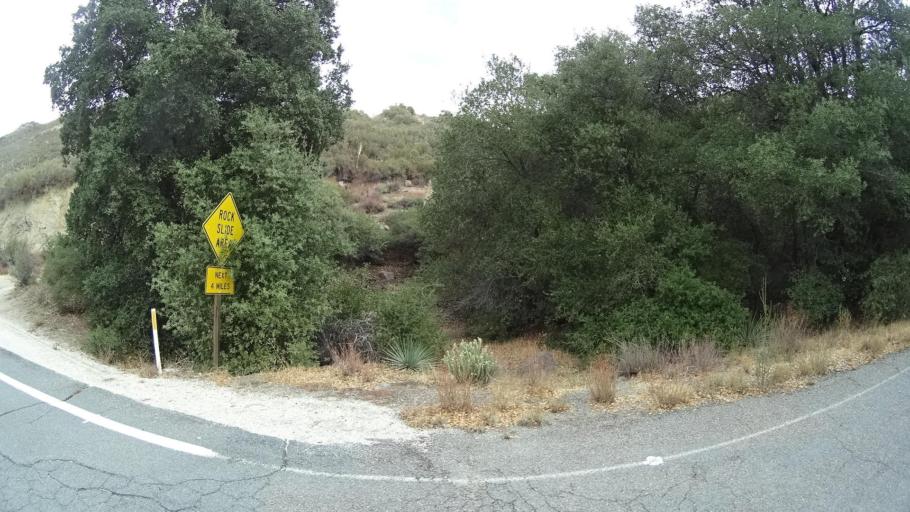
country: US
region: California
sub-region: San Diego County
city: Pine Valley
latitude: 32.7875
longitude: -116.4494
